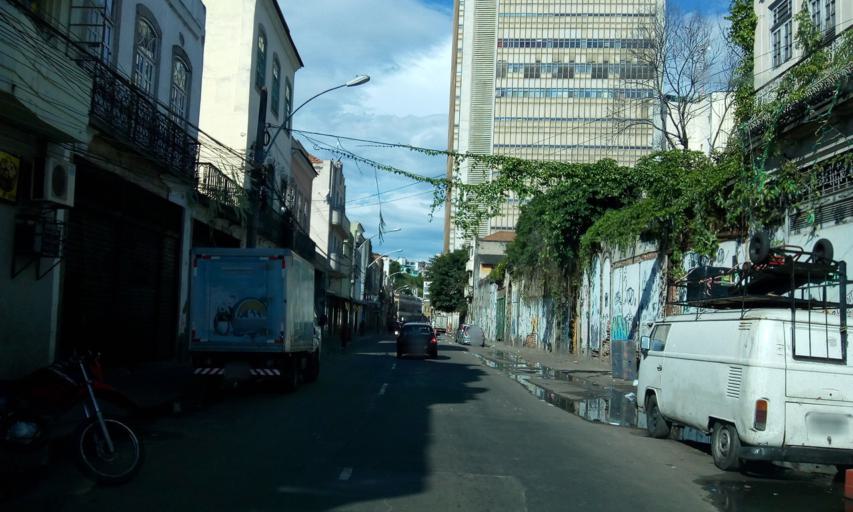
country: BR
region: Rio de Janeiro
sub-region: Rio De Janeiro
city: Rio de Janeiro
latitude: -22.9013
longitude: -43.1894
